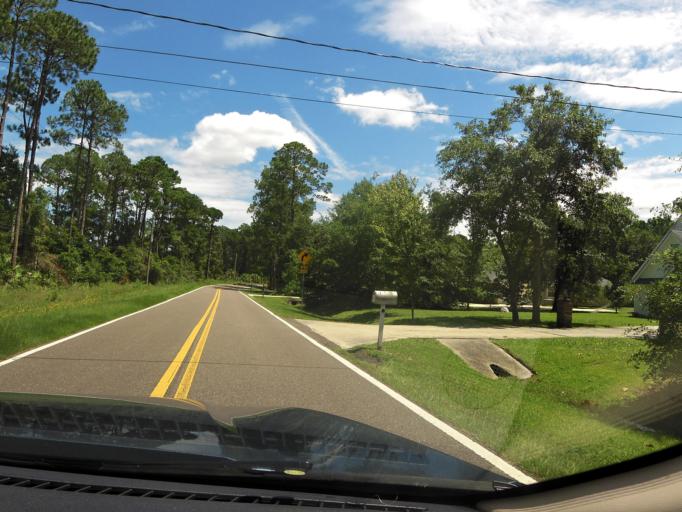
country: US
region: Georgia
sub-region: Camden County
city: St. Marys
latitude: 30.6768
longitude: -81.5317
